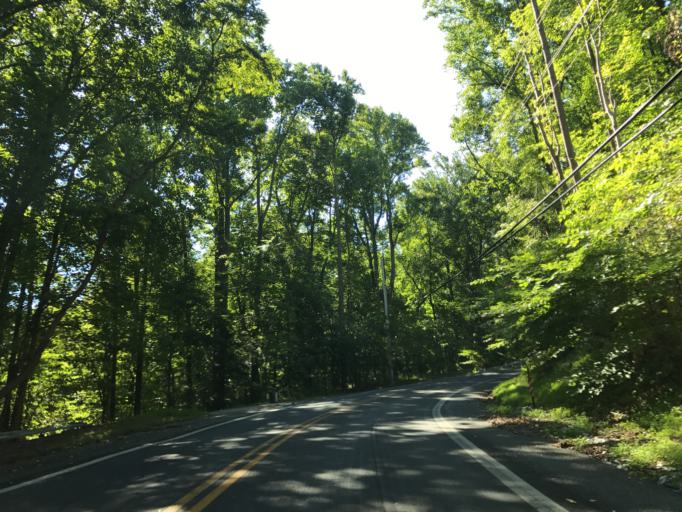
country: US
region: Maryland
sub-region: Howard County
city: Ilchester
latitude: 39.2470
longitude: -76.7677
